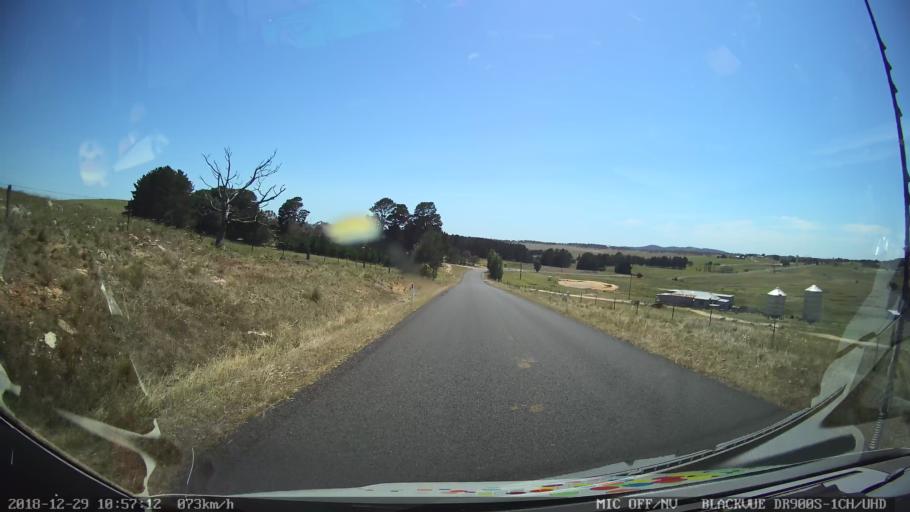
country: AU
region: New South Wales
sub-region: Palerang
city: Bungendore
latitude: -35.1380
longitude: 149.5452
